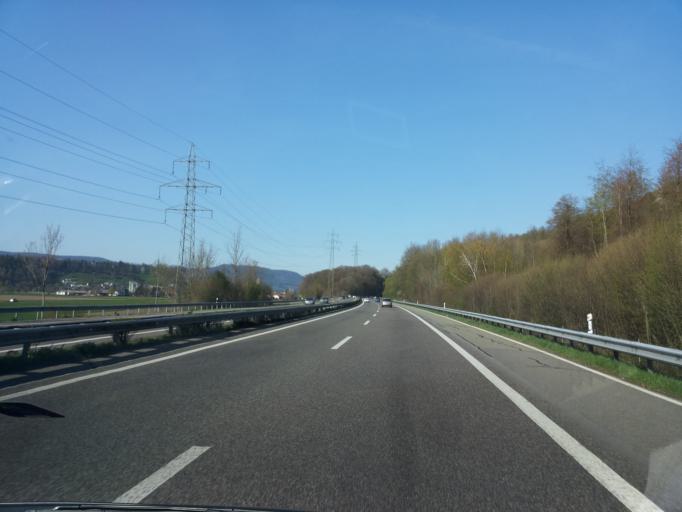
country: CH
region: Aargau
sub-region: Bezirk Aarau
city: Oberentfelden
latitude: 47.3570
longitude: 8.0636
